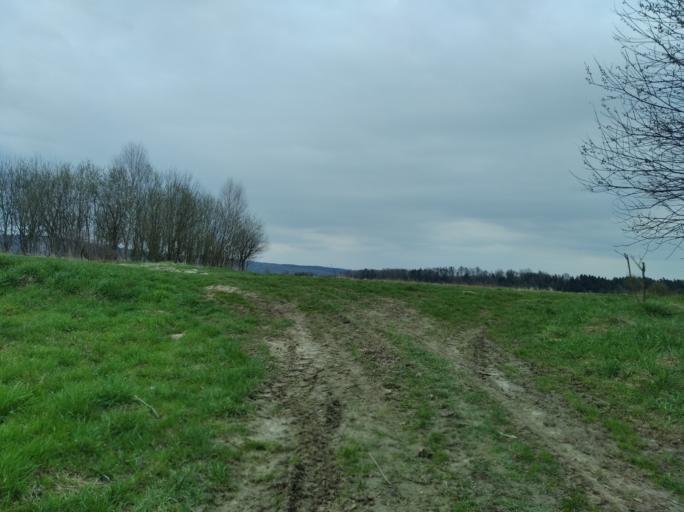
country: PL
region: Subcarpathian Voivodeship
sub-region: Powiat strzyzowski
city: Strzyzow
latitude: 49.8483
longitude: 21.7882
